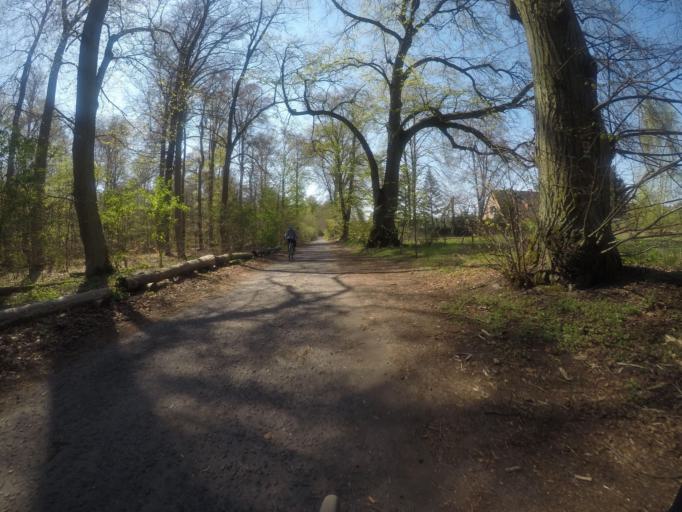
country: DE
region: Brandenburg
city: Wandlitz
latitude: 52.7531
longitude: 13.5158
